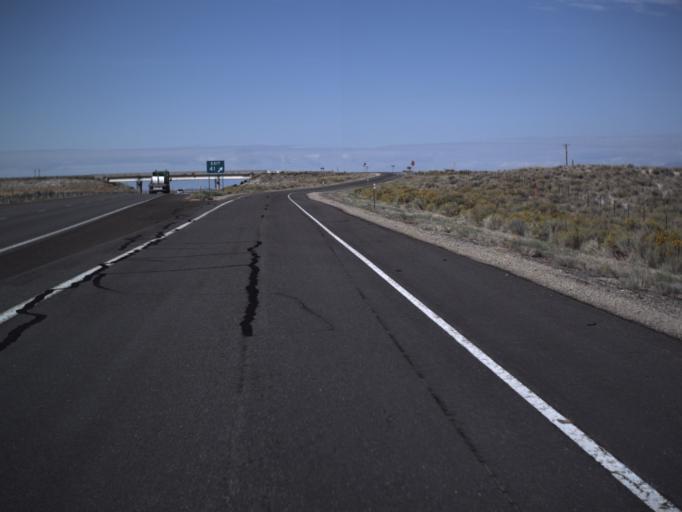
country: US
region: Utah
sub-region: Tooele County
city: Wendover
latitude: 40.7274
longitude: -113.2533
